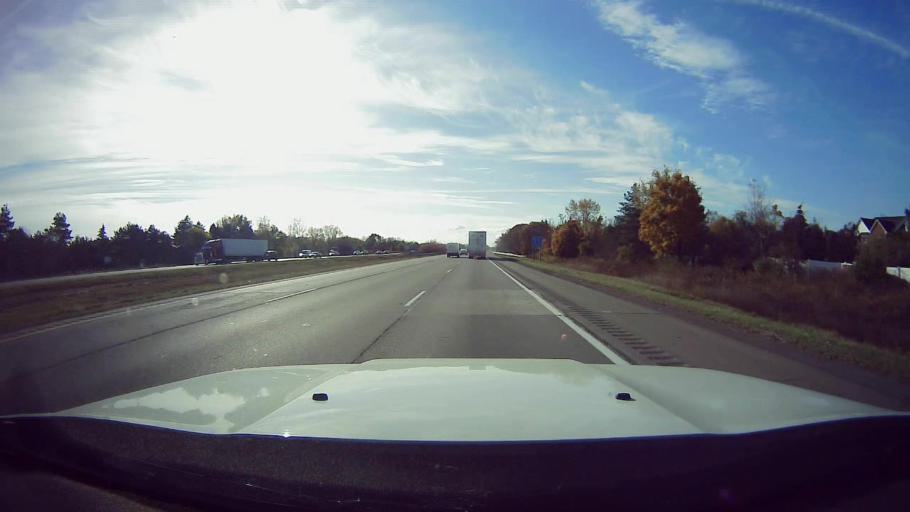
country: US
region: Michigan
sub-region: Wayne County
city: Canton
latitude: 42.3078
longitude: -83.4429
